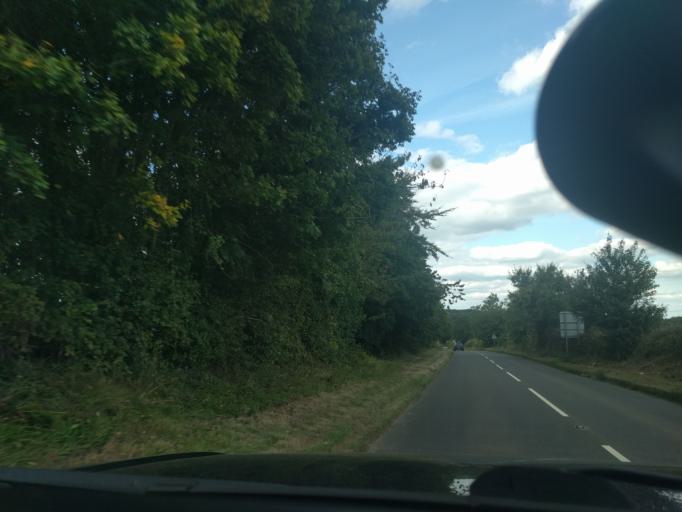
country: GB
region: England
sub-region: Wiltshire
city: Box
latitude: 51.4102
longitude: -2.2311
